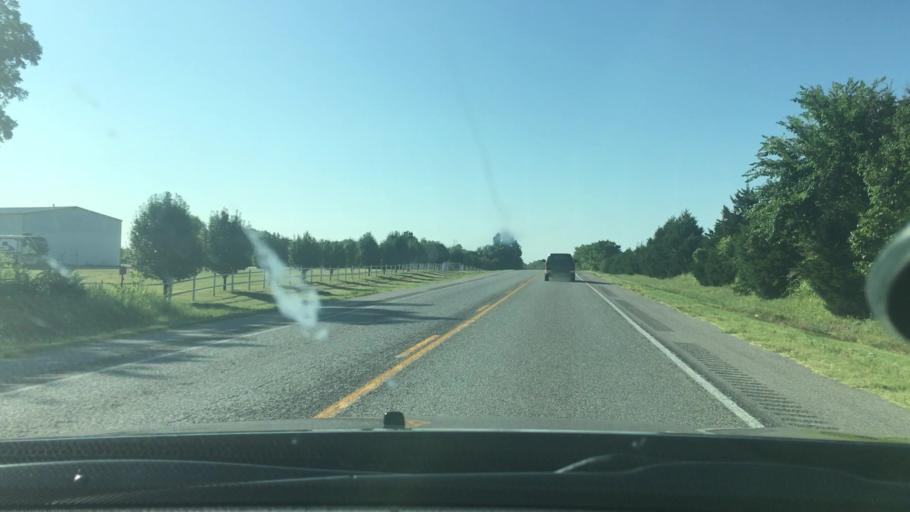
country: US
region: Oklahoma
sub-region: Johnston County
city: Tishomingo
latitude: 34.2515
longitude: -96.7609
